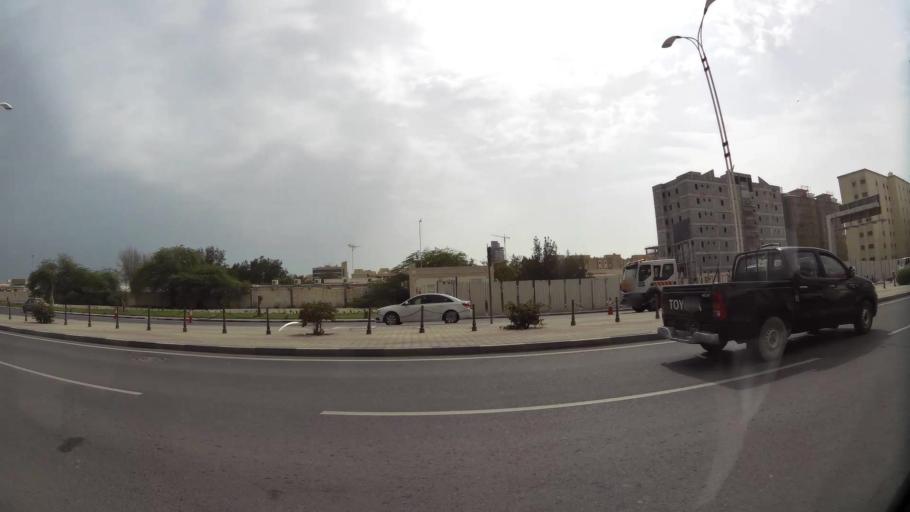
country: QA
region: Baladiyat ad Dawhah
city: Doha
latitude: 25.2889
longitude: 51.5060
